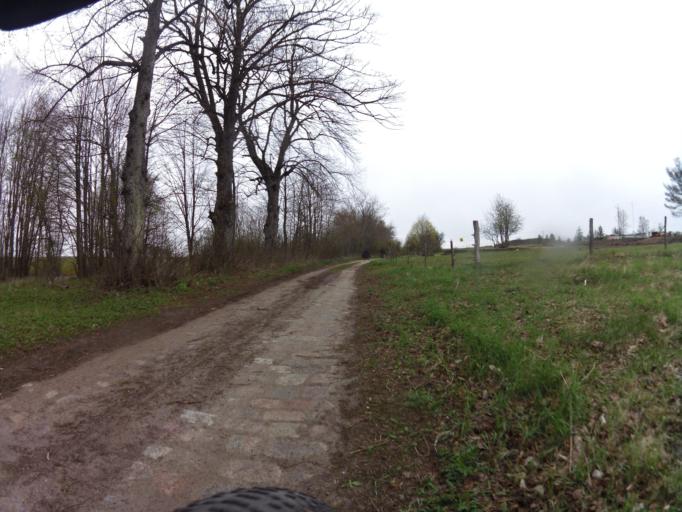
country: PL
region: West Pomeranian Voivodeship
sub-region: Powiat koszalinski
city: Bobolice
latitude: 53.9936
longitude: 16.6818
